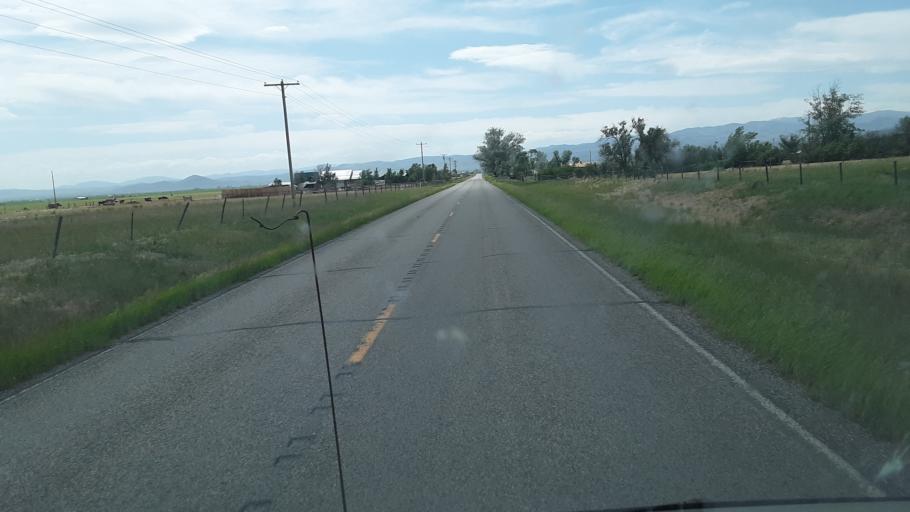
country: US
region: Montana
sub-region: Broadwater County
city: Townsend
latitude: 46.1736
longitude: -111.4592
